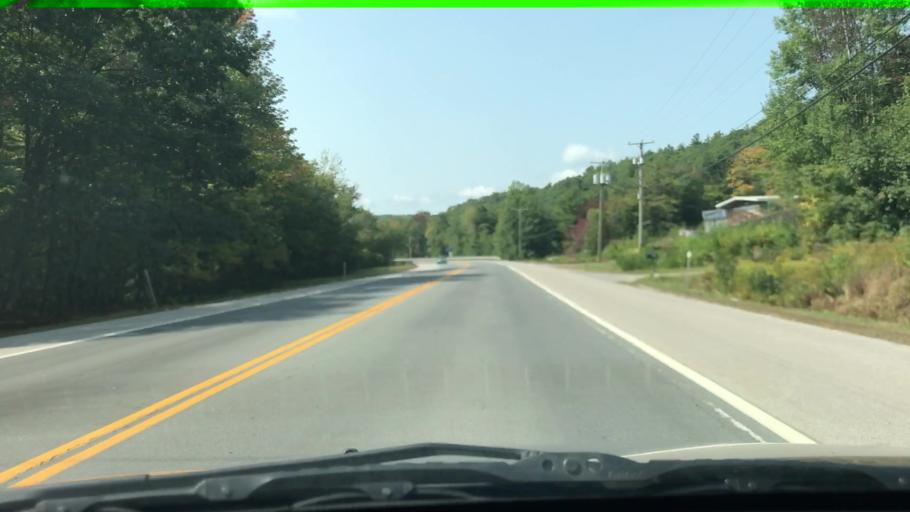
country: US
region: New Hampshire
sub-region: Cheshire County
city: Marlborough
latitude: 42.8735
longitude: -72.2193
